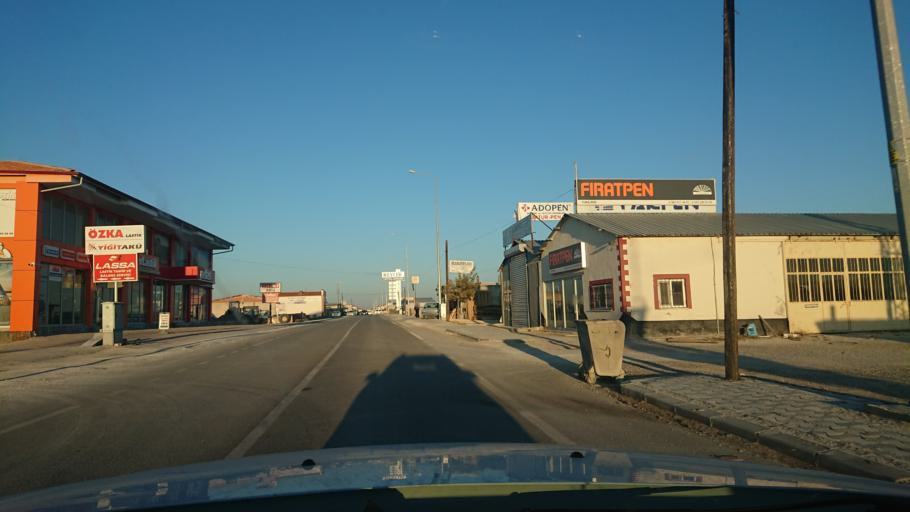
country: TR
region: Aksaray
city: Eskil
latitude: 38.3939
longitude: 33.3950
